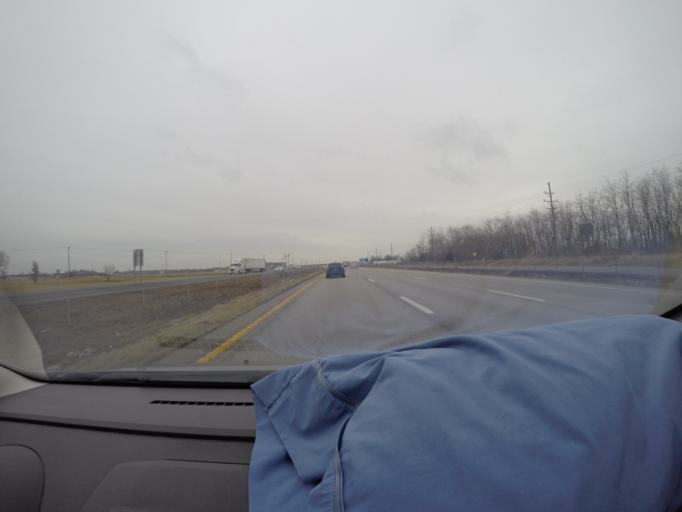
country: US
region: Missouri
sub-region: Warren County
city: Wright City
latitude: 38.8281
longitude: -91.0487
